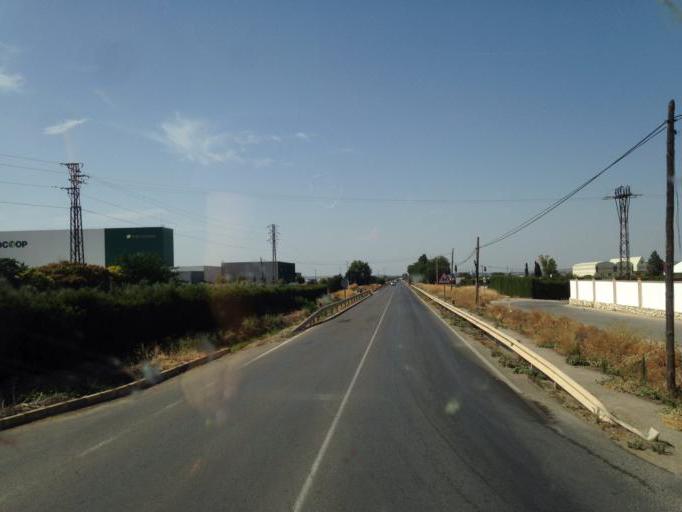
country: ES
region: Andalusia
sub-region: Provincia de Malaga
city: Antequera
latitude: 37.0349
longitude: -4.5612
